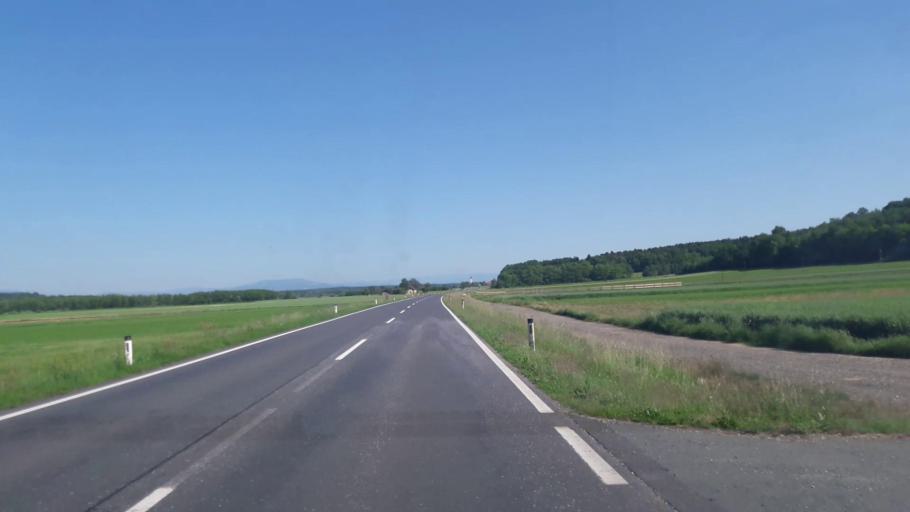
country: AT
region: Burgenland
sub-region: Politischer Bezirk Jennersdorf
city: Rudersdorf
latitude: 47.0621
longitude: 16.1159
